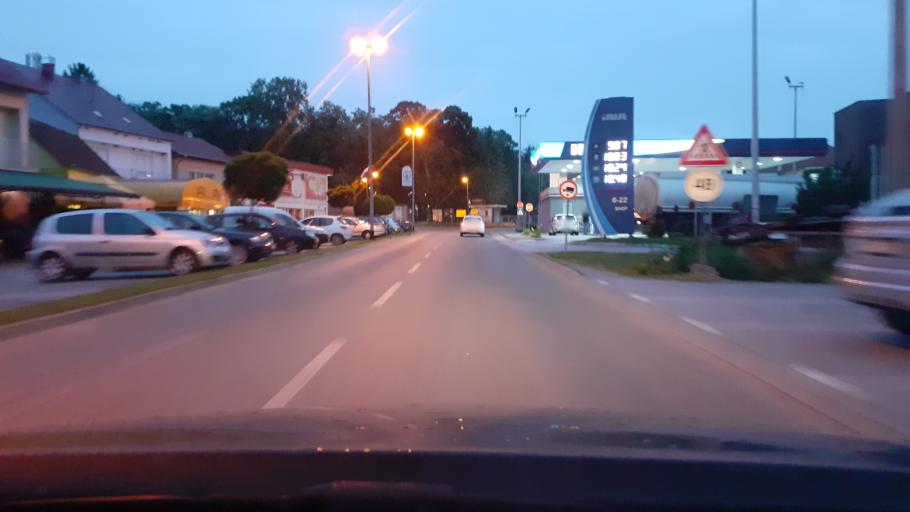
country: HR
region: Pozesko-Slavonska
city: Pleternica
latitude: 45.2856
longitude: 17.8037
